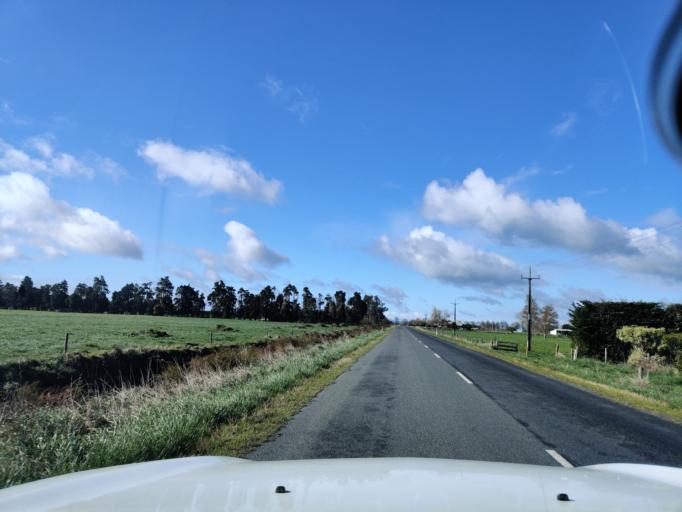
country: NZ
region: Waikato
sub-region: Waikato District
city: Ngaruawahia
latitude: -37.5993
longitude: 175.2989
